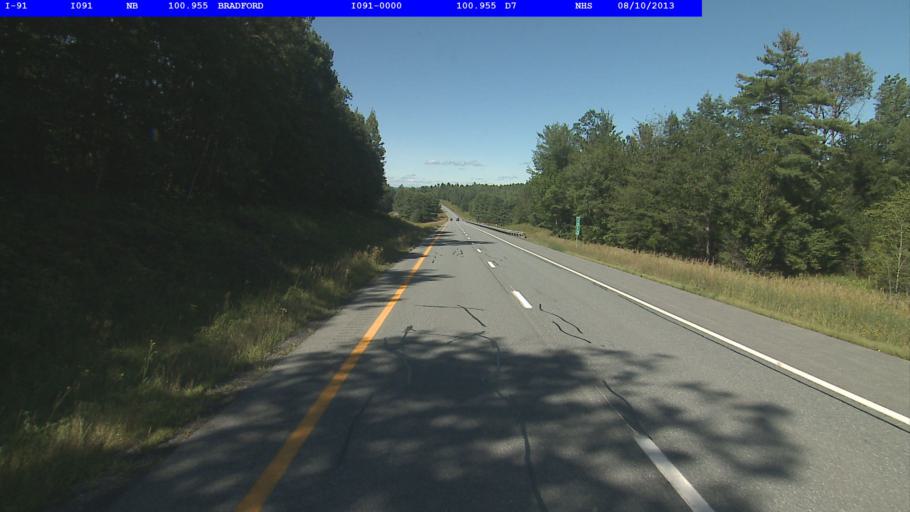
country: US
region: New Hampshire
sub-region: Grafton County
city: Haverhill
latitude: 44.0280
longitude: -72.1141
